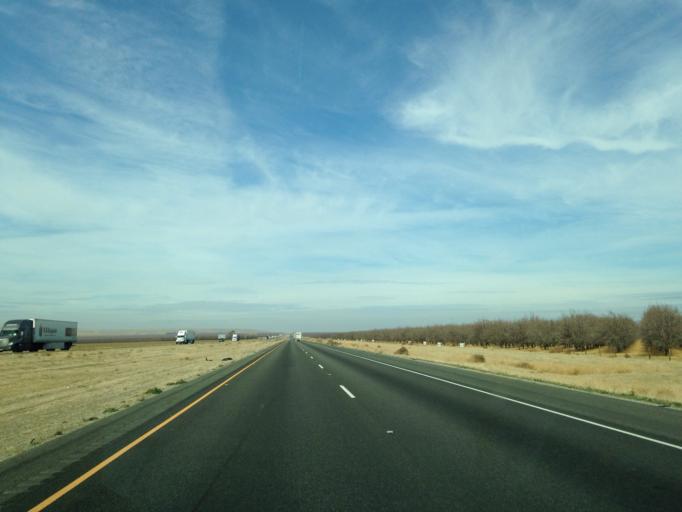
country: US
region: California
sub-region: Merced County
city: South Dos Palos
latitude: 36.7911
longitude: -120.7331
